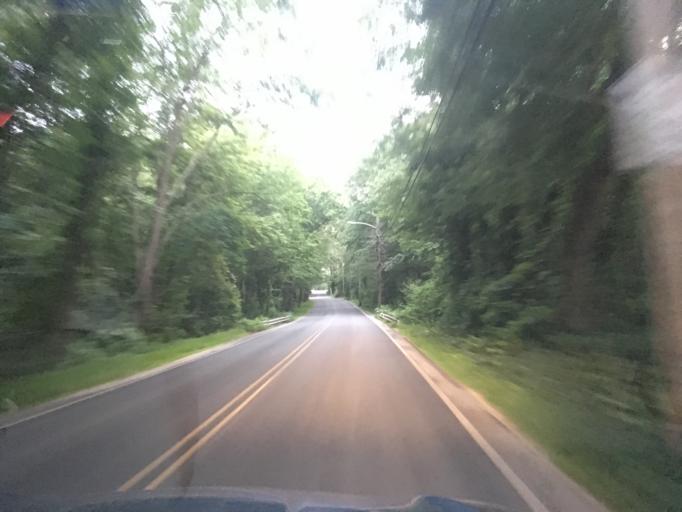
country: US
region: Rhode Island
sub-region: Washington County
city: Exeter
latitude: 41.6302
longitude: -71.5137
